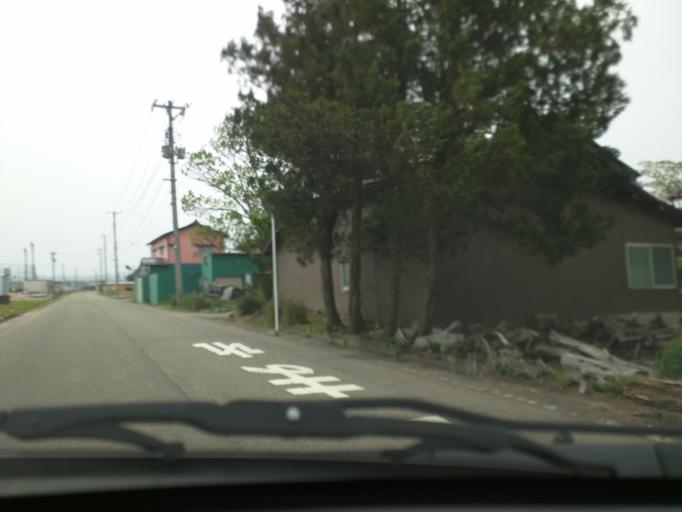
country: JP
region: Niigata
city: Mitsuke
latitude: 37.5514
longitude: 138.9116
